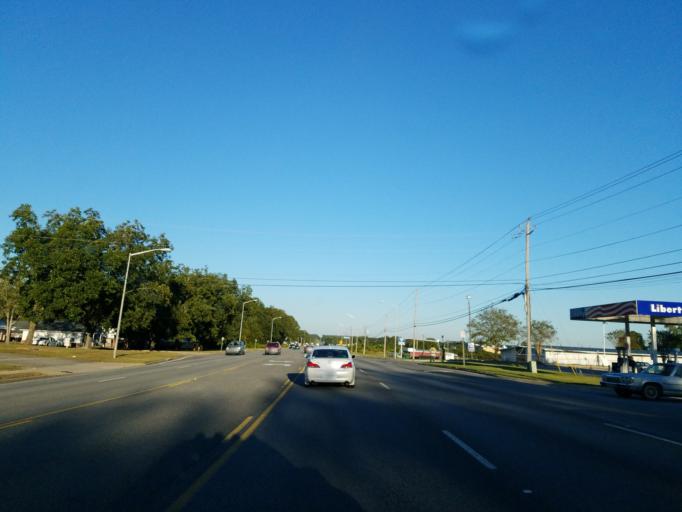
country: US
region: Georgia
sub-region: Worth County
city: Sylvester
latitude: 31.5273
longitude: -83.8167
